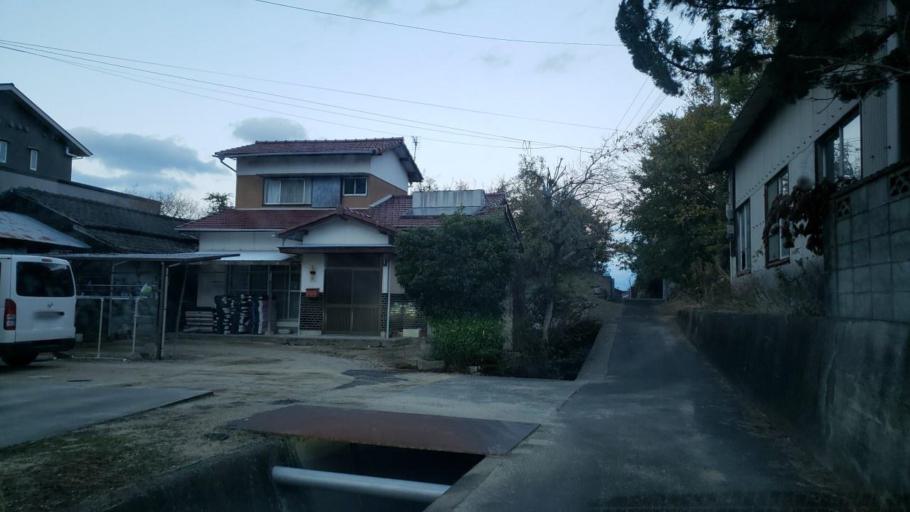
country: JP
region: Tokushima
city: Kamojimacho-jogejima
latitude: 34.2342
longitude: 134.3474
